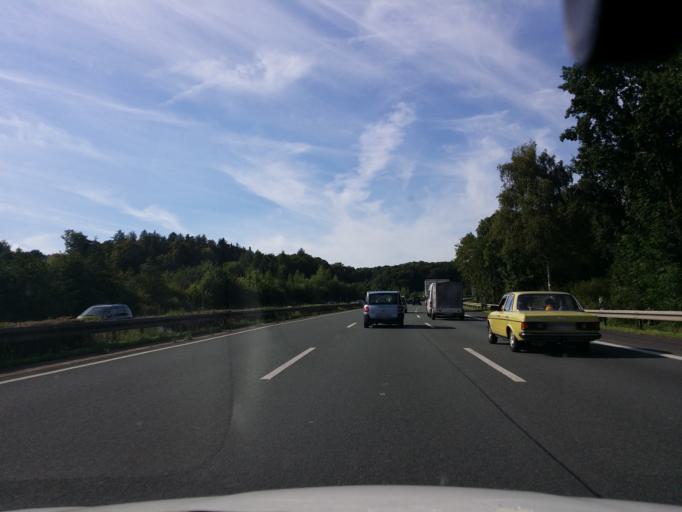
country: DE
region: North Rhine-Westphalia
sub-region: Regierungsbezirk Koln
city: Bad Honnef
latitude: 50.6790
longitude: 7.2832
